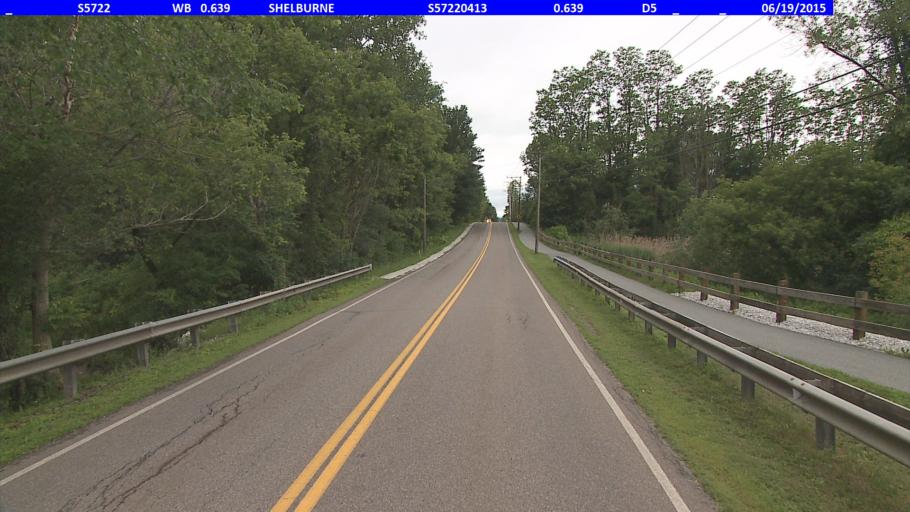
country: US
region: Vermont
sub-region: Chittenden County
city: Burlington
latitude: 44.3895
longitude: -73.2125
